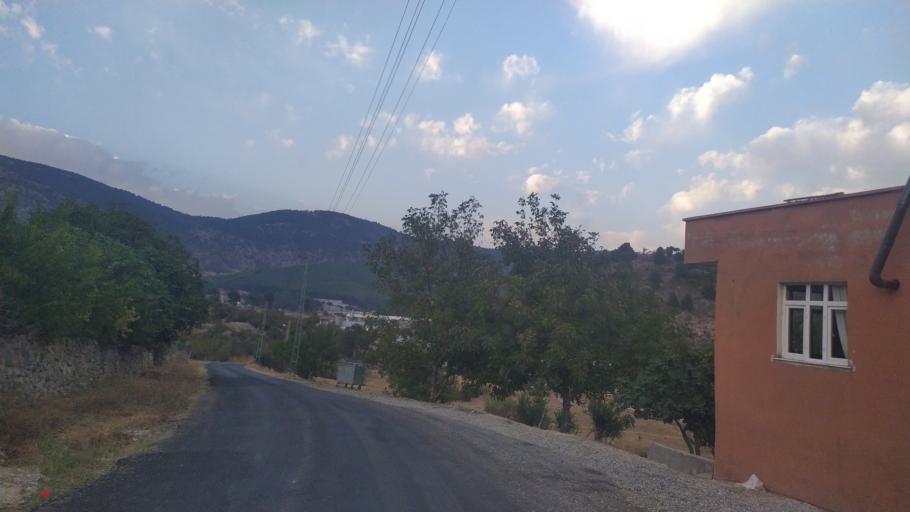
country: TR
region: Mersin
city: Camliyayla
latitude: 37.2312
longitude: 34.7151
